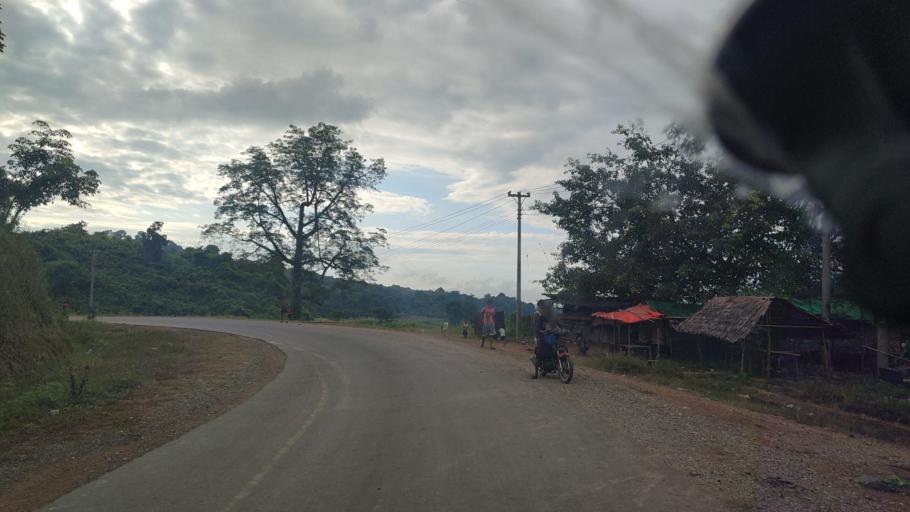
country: MM
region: Magway
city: Minbu
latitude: 19.7617
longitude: 94.0387
